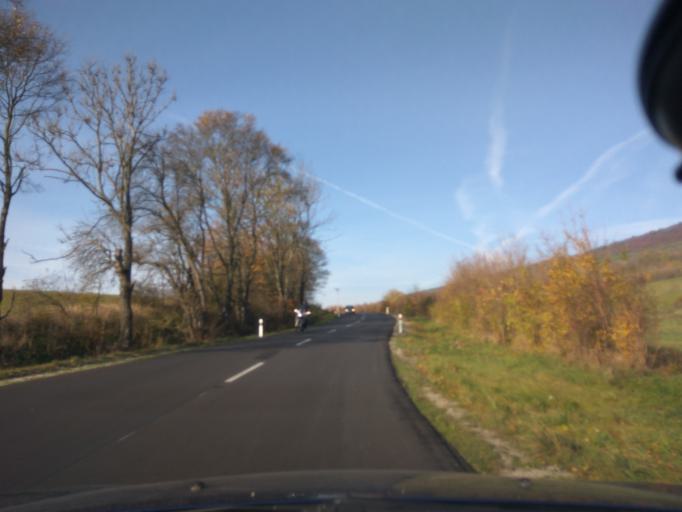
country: SK
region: Nitriansky
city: Brezova pod Bradlom
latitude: 48.6704
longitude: 17.5652
